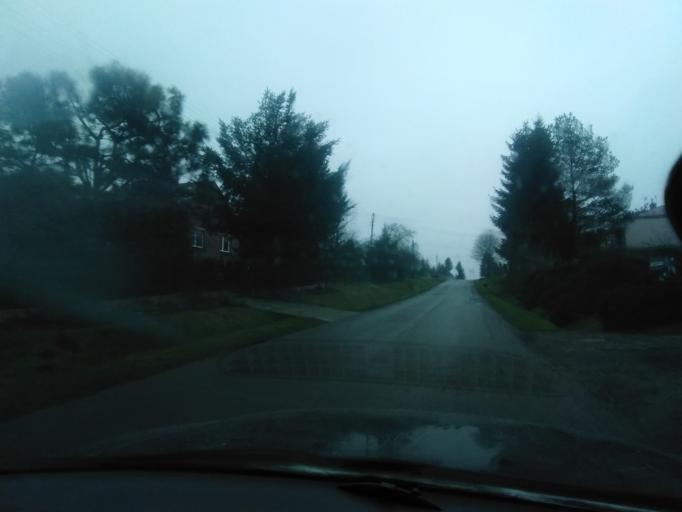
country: PL
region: Subcarpathian Voivodeship
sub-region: Powiat jaroslawski
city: Rokietnica
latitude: 49.9466
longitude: 22.6074
